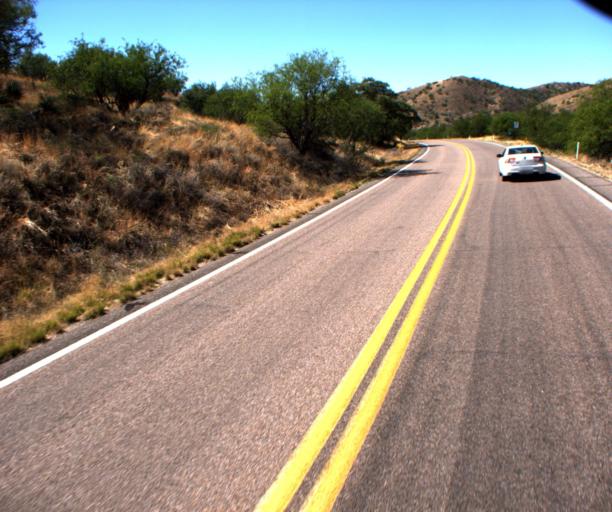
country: US
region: Arizona
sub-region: Santa Cruz County
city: Rio Rico
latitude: 31.4904
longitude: -110.8160
